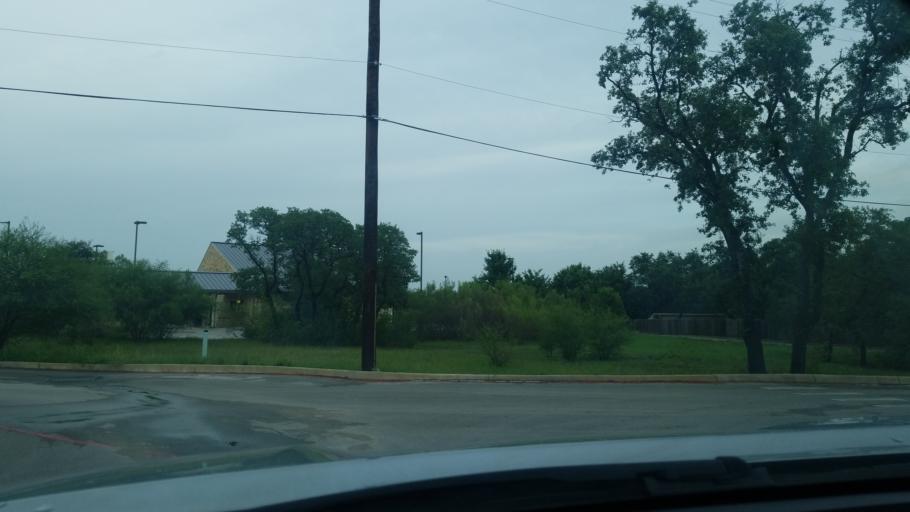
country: US
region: Texas
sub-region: Bexar County
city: Shavano Park
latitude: 29.6069
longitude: -98.5239
